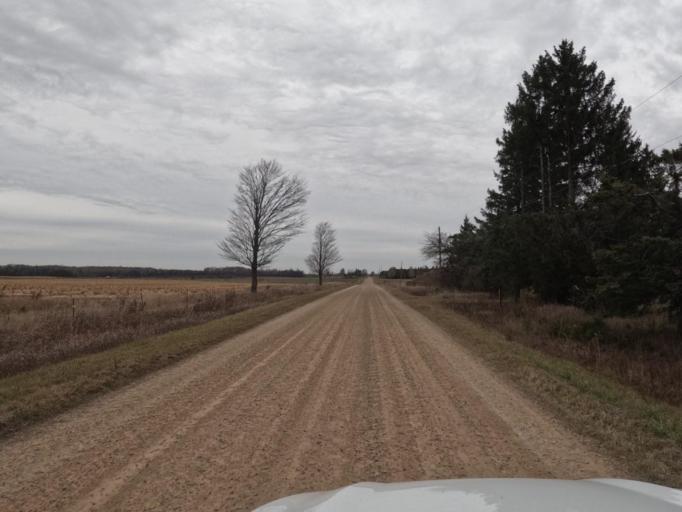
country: CA
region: Ontario
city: Shelburne
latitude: 44.0175
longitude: -80.3683
